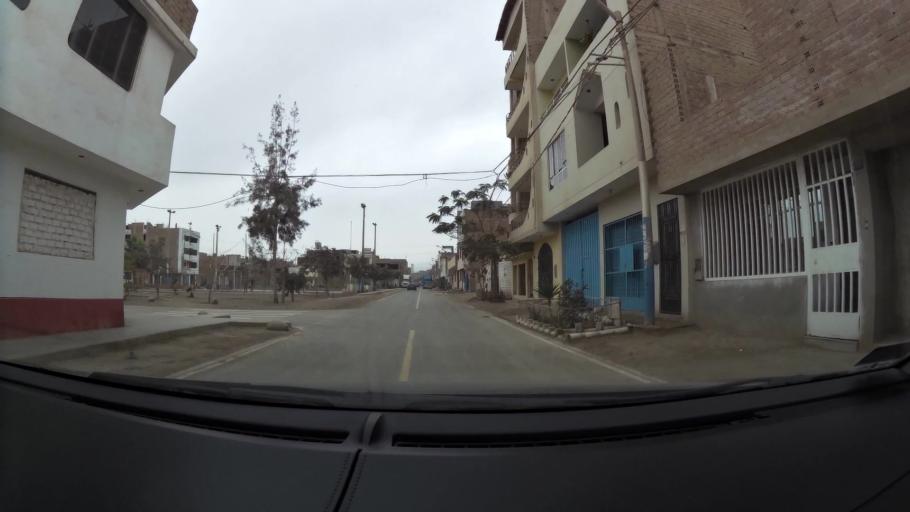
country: PE
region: Lima
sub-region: Lima
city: Independencia
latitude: -11.9721
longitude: -77.0935
